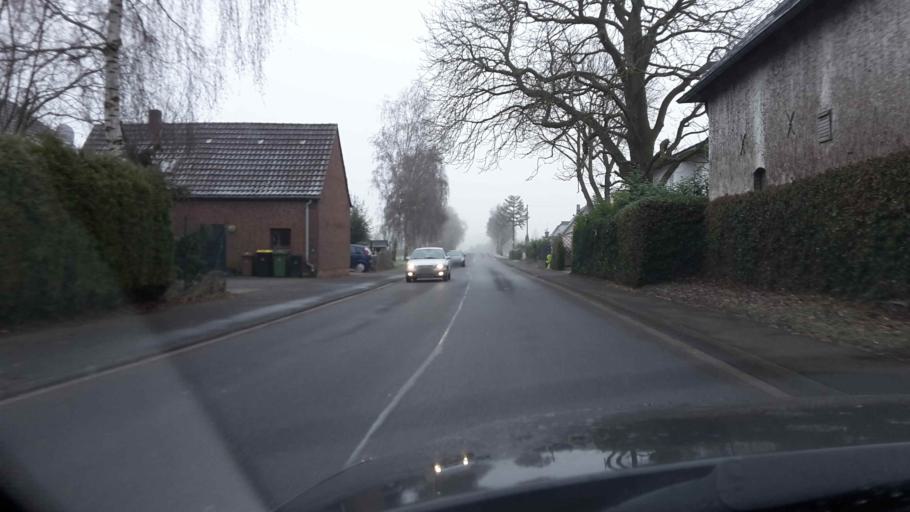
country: DE
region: North Rhine-Westphalia
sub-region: Regierungsbezirk Koln
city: Hennef
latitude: 50.7485
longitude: 7.2829
